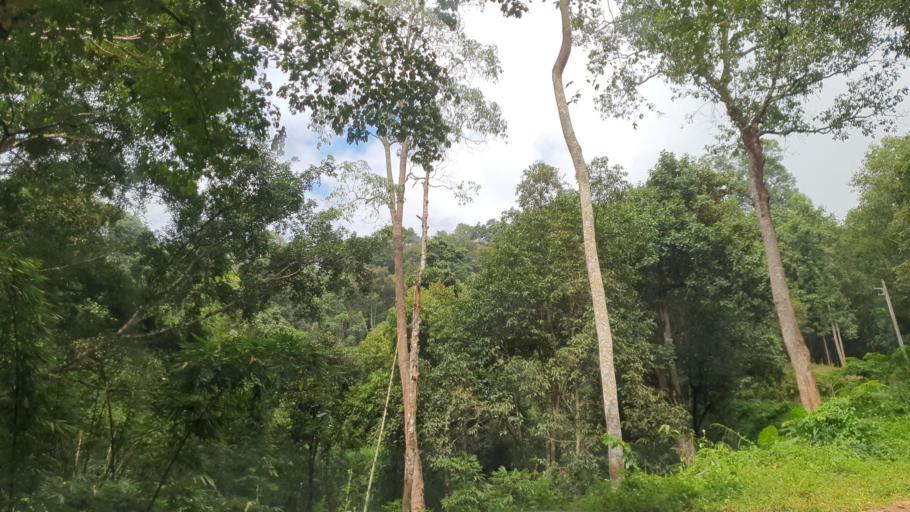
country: TH
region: Chiang Mai
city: Mae On
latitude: 18.9460
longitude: 99.3083
